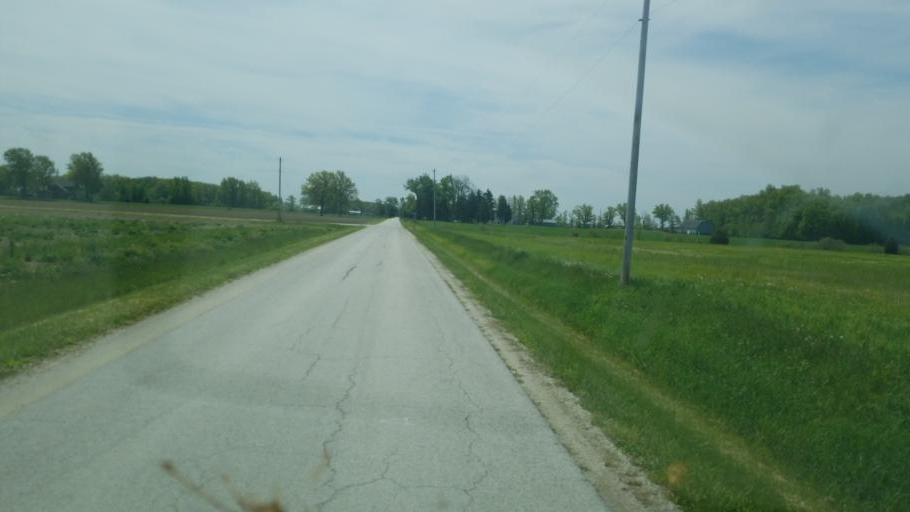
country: US
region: Ohio
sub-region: Ottawa County
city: Oak Harbor
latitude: 41.4879
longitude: -83.1642
